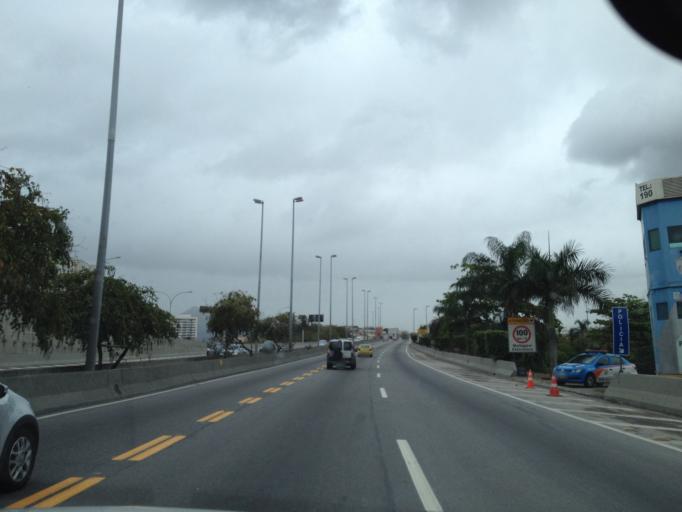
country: BR
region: Rio de Janeiro
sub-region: Rio De Janeiro
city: Rio de Janeiro
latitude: -22.8819
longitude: -43.2839
